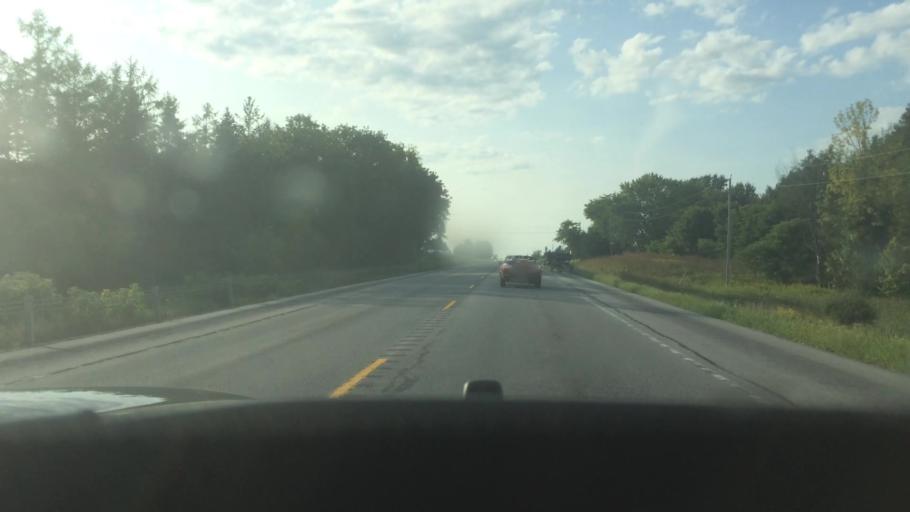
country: US
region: New York
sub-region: St. Lawrence County
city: Canton
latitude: 44.6234
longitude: -75.2330
